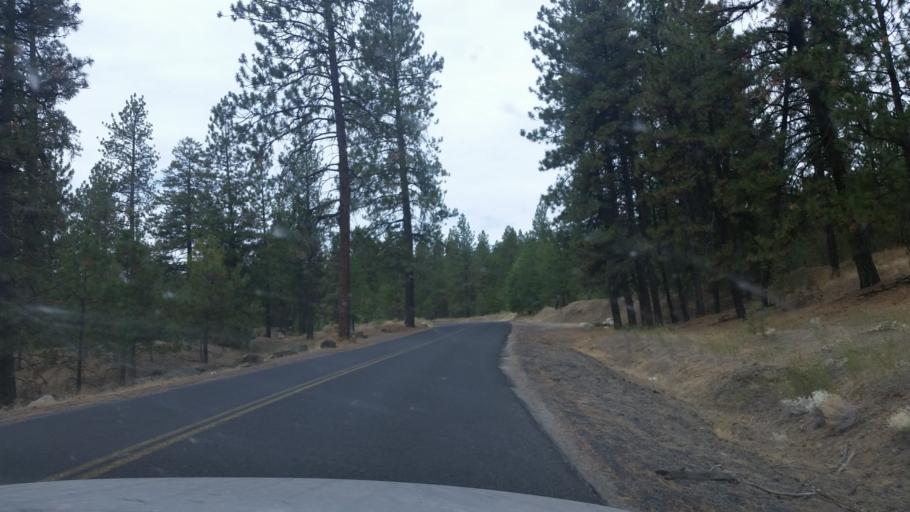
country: US
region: Washington
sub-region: Spokane County
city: Spokane
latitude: 47.6547
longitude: -117.4784
